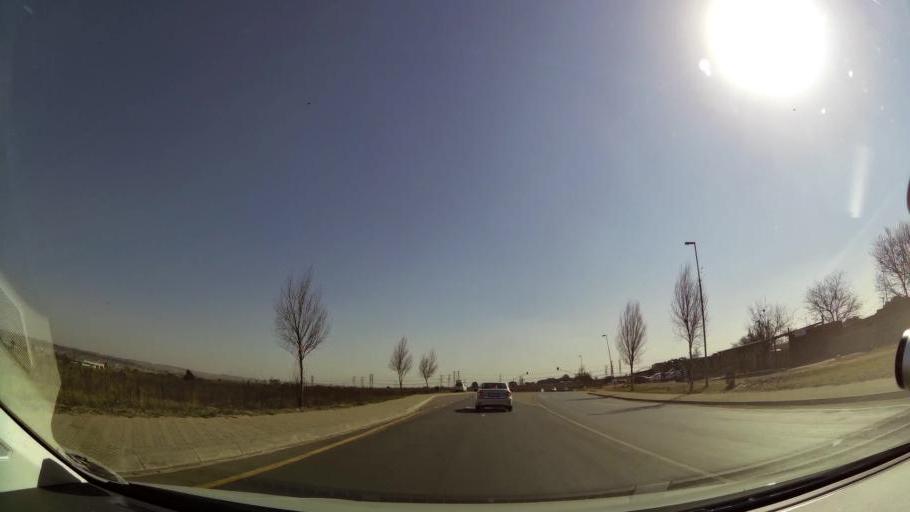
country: ZA
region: Gauteng
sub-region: Ekurhuleni Metropolitan Municipality
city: Tembisa
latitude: -26.0289
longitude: 28.2364
